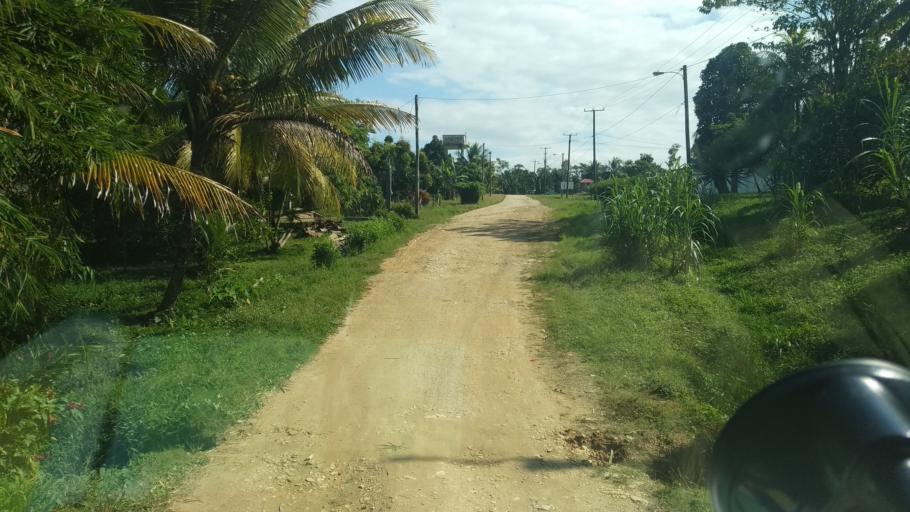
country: BZ
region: Toledo
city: Punta Gorda
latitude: 16.2161
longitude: -88.9058
